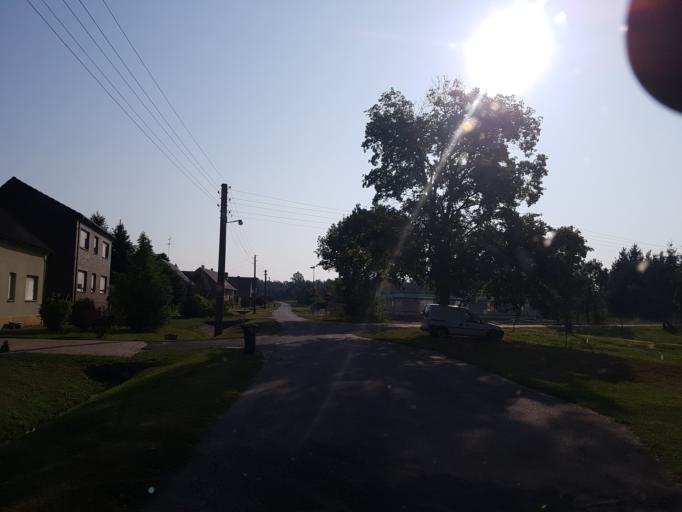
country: DE
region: Brandenburg
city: Finsterwalde
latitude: 51.6869
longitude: 13.7216
